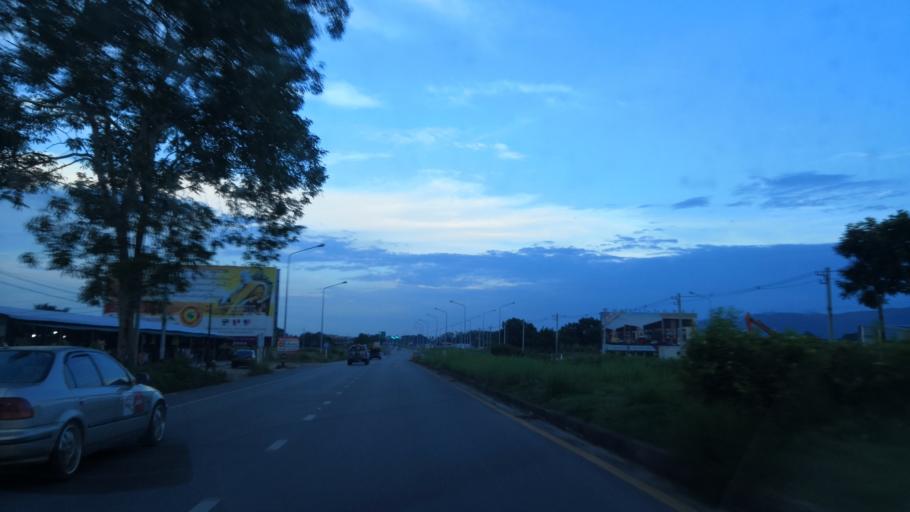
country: TH
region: Chiang Rai
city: Chiang Rai
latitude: 19.8487
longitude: 99.8101
